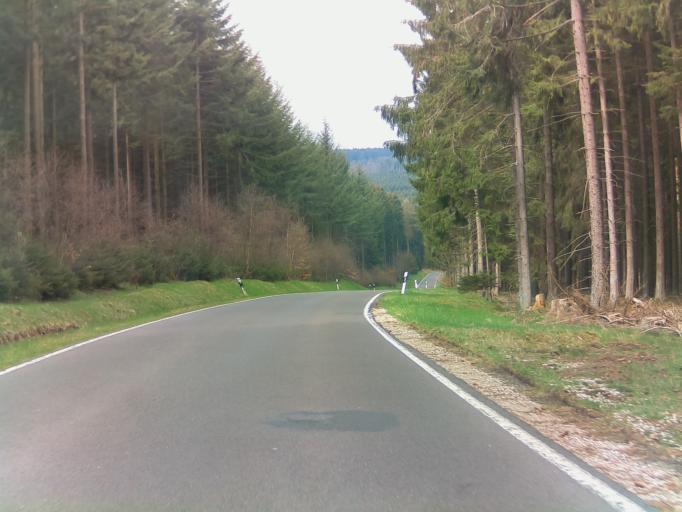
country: DE
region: Rheinland-Pfalz
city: Bruchweiler
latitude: 49.8095
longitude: 7.2179
